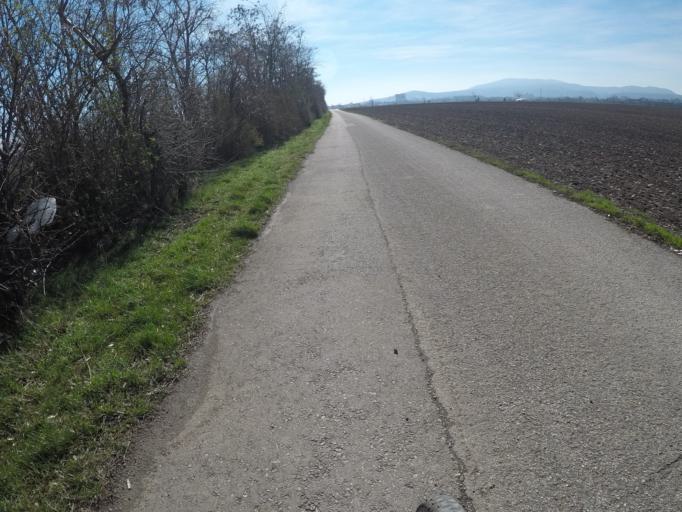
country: AT
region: Lower Austria
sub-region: Politischer Bezirk Modling
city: Vosendorf
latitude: 48.1094
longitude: 16.3332
